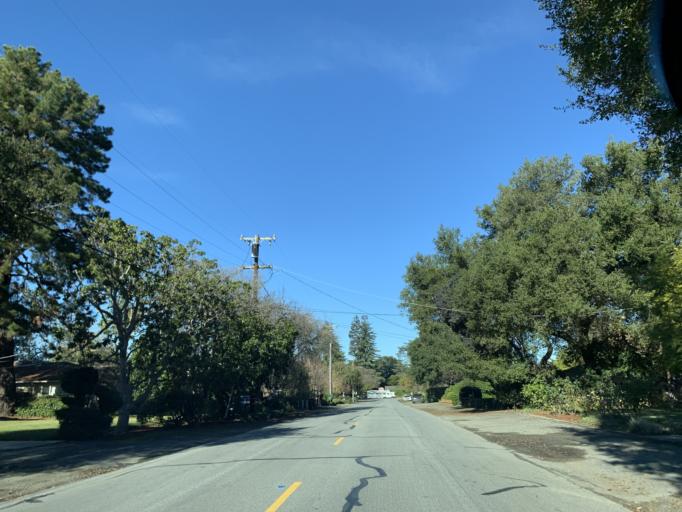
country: US
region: California
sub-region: Santa Clara County
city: Los Altos
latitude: 37.3833
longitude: -122.1001
